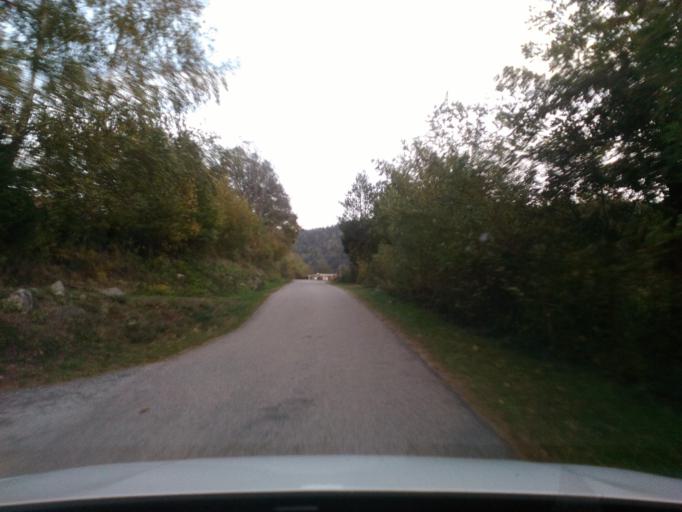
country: FR
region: Lorraine
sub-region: Departement des Vosges
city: Le Tholy
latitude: 48.0697
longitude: 6.7267
